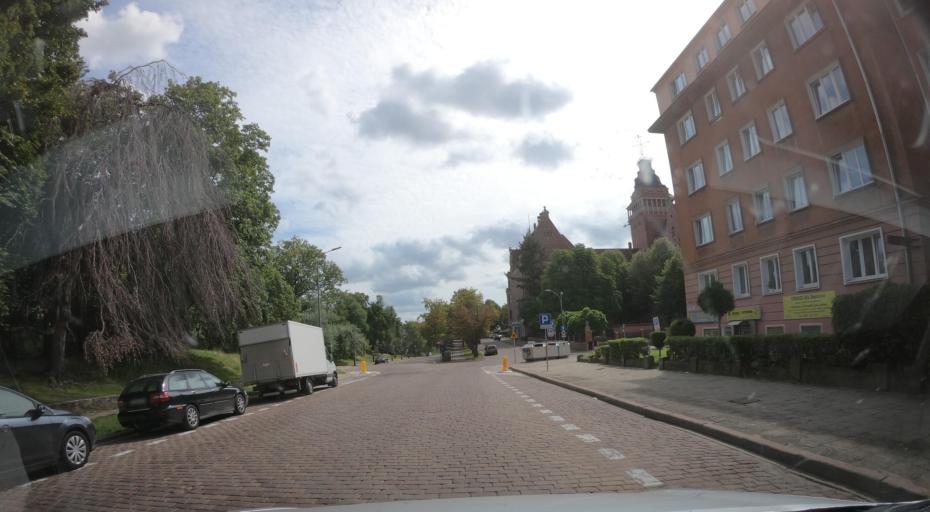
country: PL
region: West Pomeranian Voivodeship
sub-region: Szczecin
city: Szczecin
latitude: 53.4324
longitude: 14.5658
